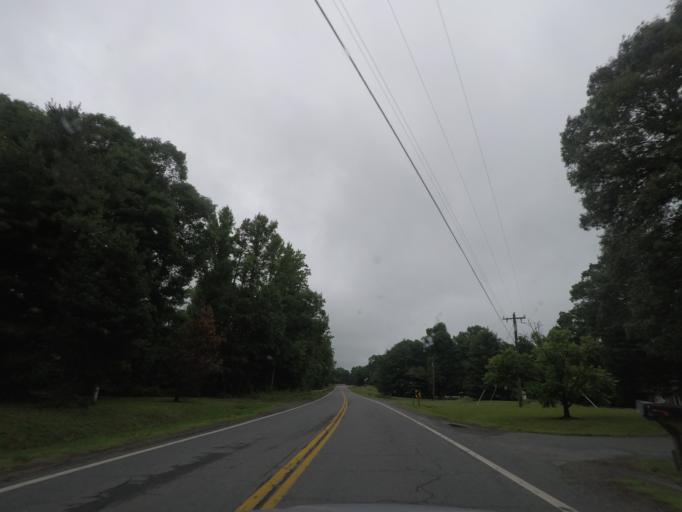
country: US
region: Virginia
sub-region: Fluvanna County
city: Weber City
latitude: 37.6607
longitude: -78.3481
